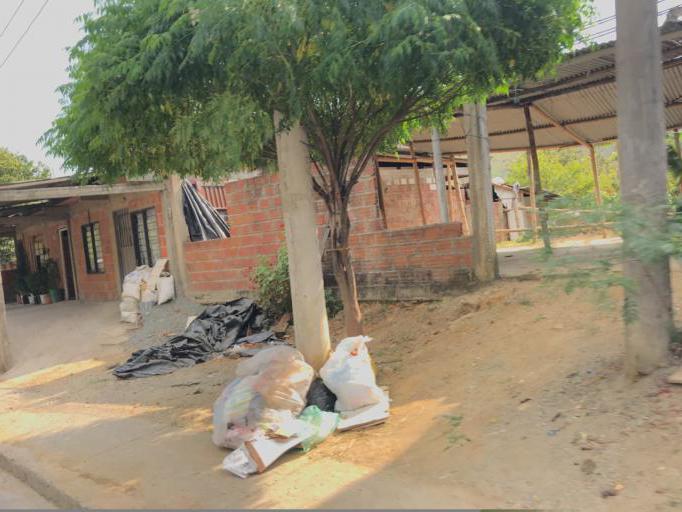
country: CO
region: Valle del Cauca
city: Cali
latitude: 3.4507
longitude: -76.5598
